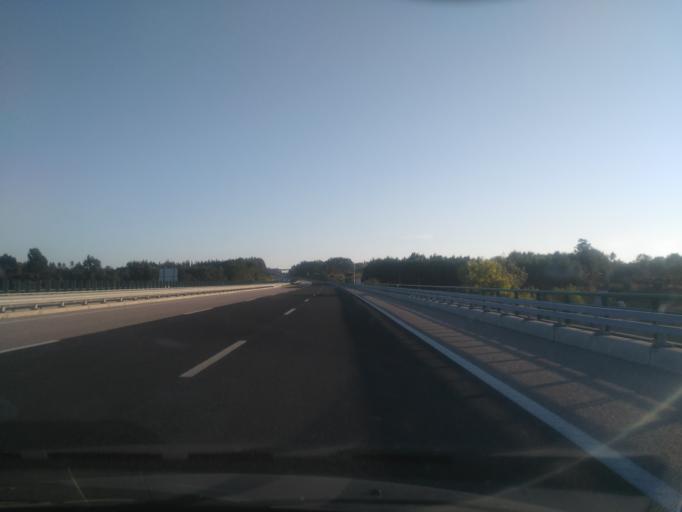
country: PT
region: Coimbra
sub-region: Figueira da Foz
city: Lavos
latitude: 40.0917
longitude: -8.7608
